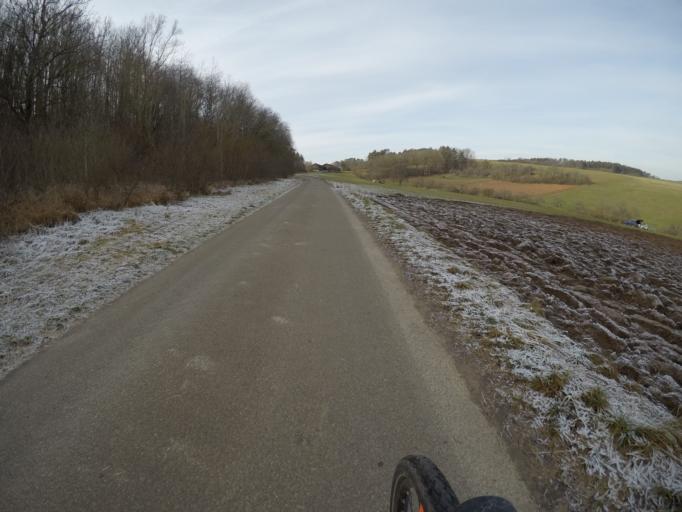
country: DE
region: Baden-Wuerttemberg
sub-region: Karlsruhe Region
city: Ostelsheim
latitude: 48.7145
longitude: 8.8764
